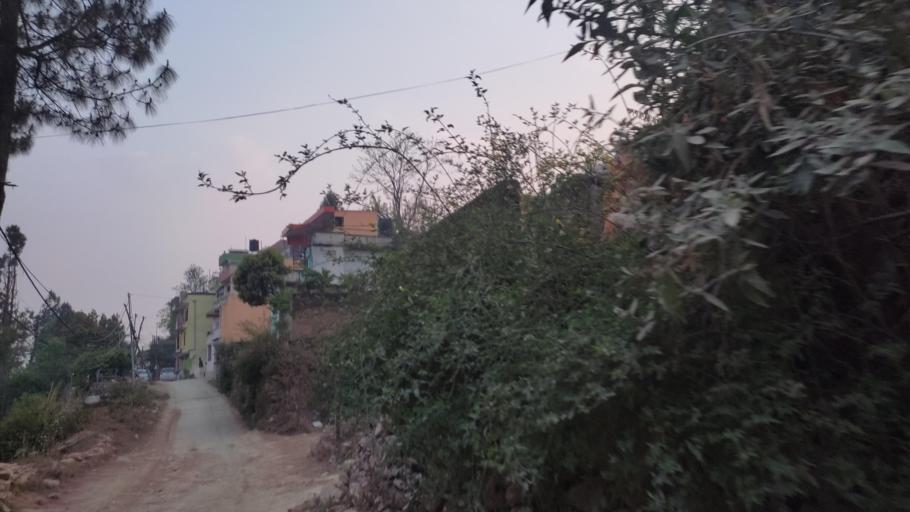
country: NP
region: Central Region
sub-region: Bagmati Zone
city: Patan
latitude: 27.6658
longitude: 85.2938
